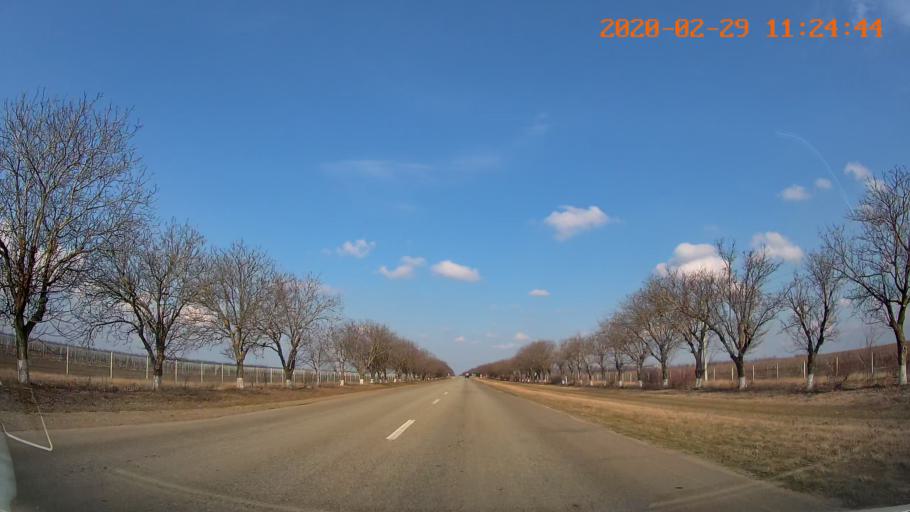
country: MD
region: Telenesti
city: Cocieri
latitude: 47.4281
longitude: 29.1534
